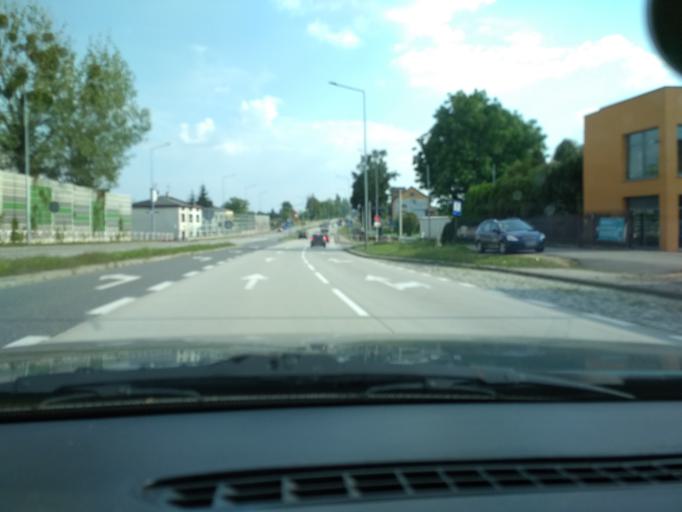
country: PL
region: Silesian Voivodeship
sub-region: Zory
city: Zory
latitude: 50.0251
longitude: 18.7073
